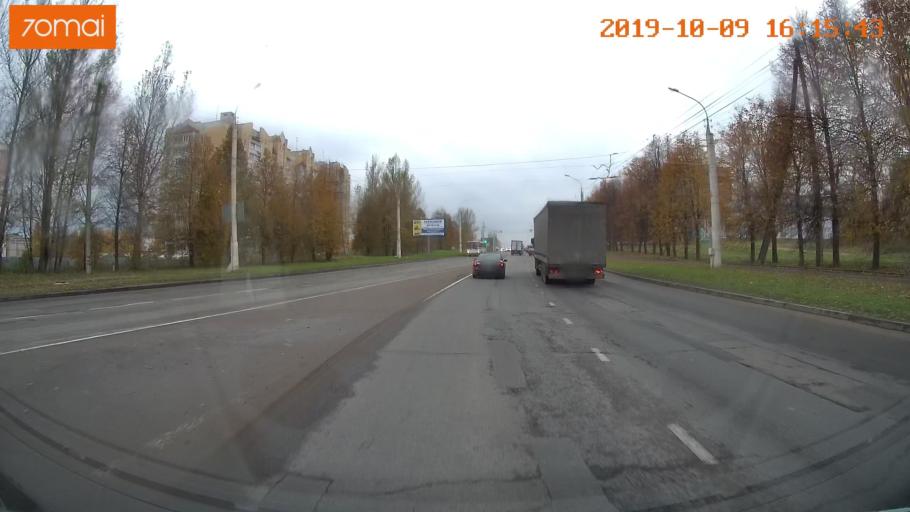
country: RU
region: Kostroma
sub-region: Kostromskoy Rayon
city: Kostroma
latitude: 57.7389
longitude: 40.9146
